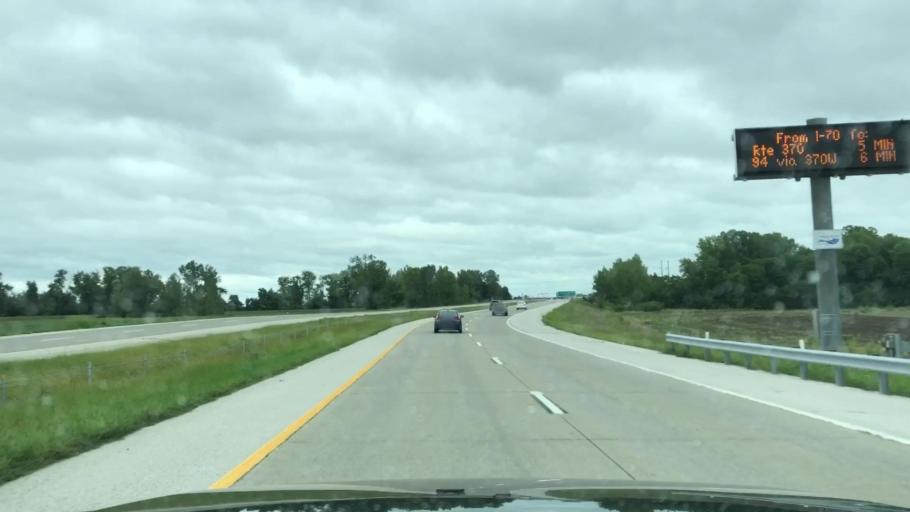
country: US
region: Missouri
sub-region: Saint Charles County
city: Saint Charles
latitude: 38.7358
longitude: -90.4790
